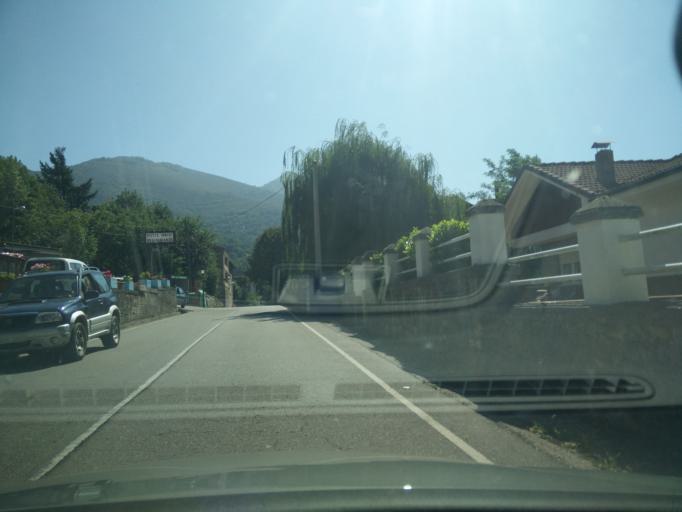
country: ES
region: Asturias
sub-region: Province of Asturias
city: Campo de Caso
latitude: 43.1816
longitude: -5.3475
